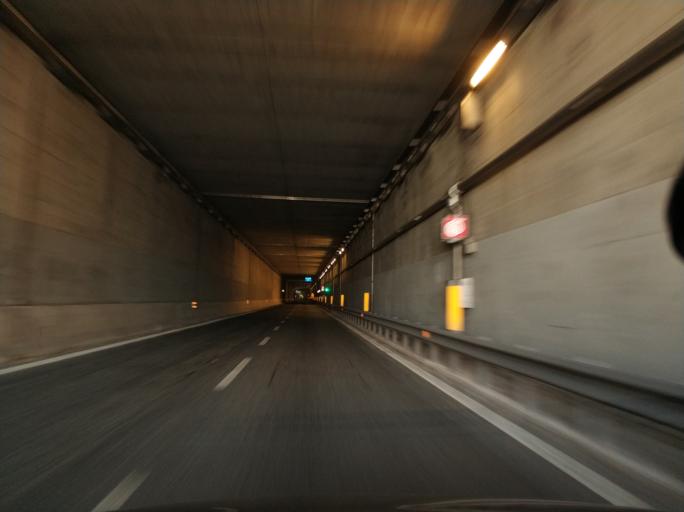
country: IT
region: Piedmont
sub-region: Provincia di Biella
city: Ponderano
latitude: 45.5483
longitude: 8.0642
